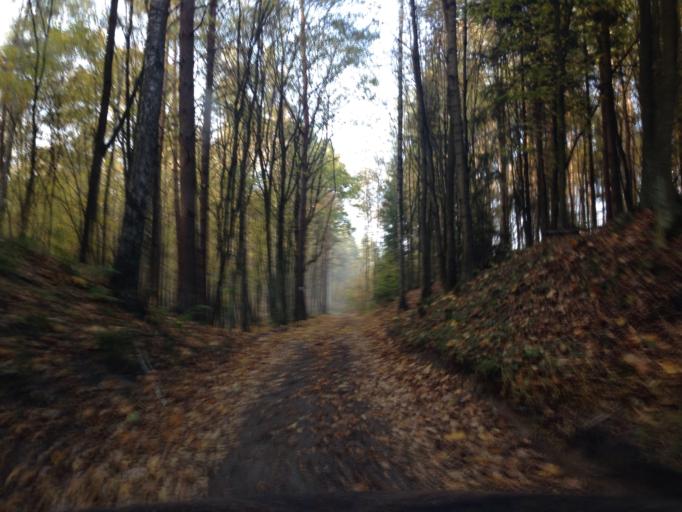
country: PL
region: Warmian-Masurian Voivodeship
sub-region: Powiat dzialdowski
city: Lidzbark
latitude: 53.2624
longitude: 19.7237
